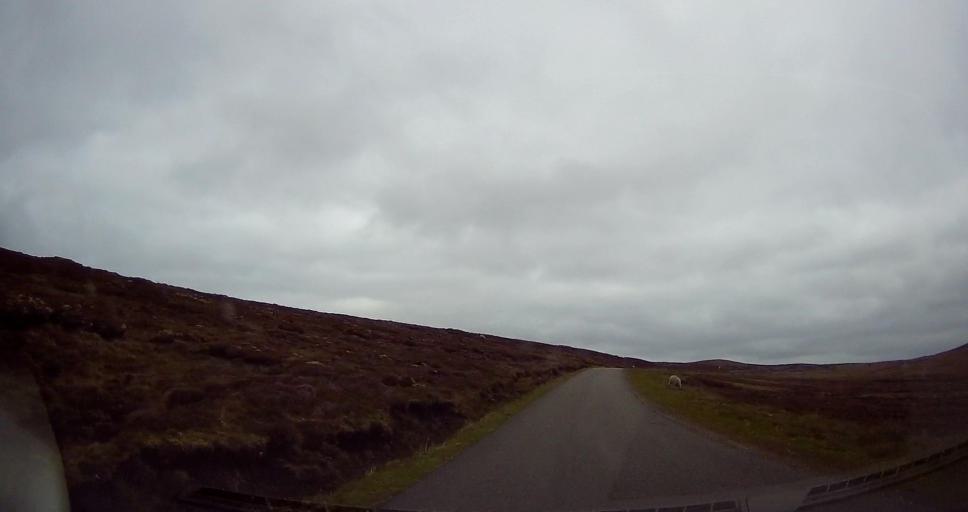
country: GB
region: Scotland
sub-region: Shetland Islands
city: Lerwick
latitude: 60.3128
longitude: -1.3416
